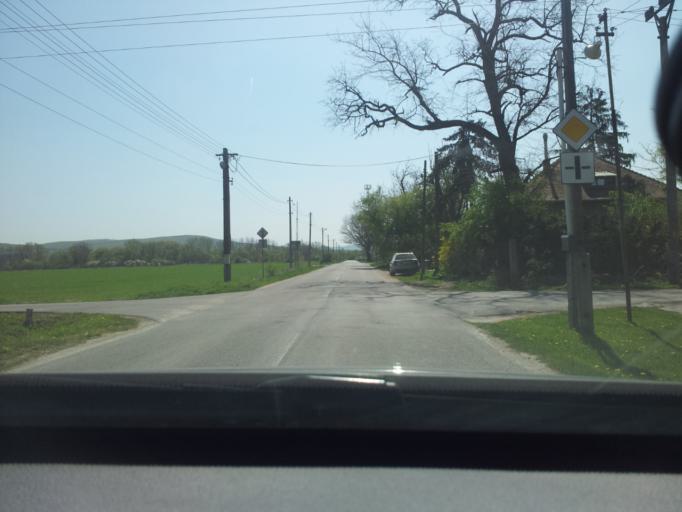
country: SK
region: Nitriansky
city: Partizanske
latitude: 48.6059
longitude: 18.2818
